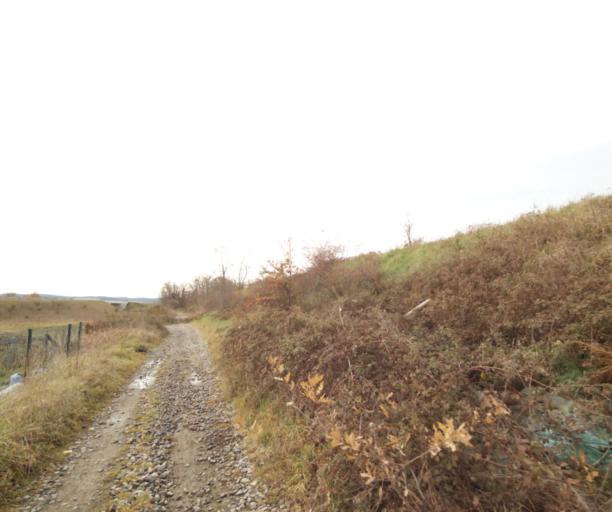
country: FR
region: Rhone-Alpes
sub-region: Departement de la Loire
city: Sury-le-Comtal
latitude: 45.5261
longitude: 4.1948
